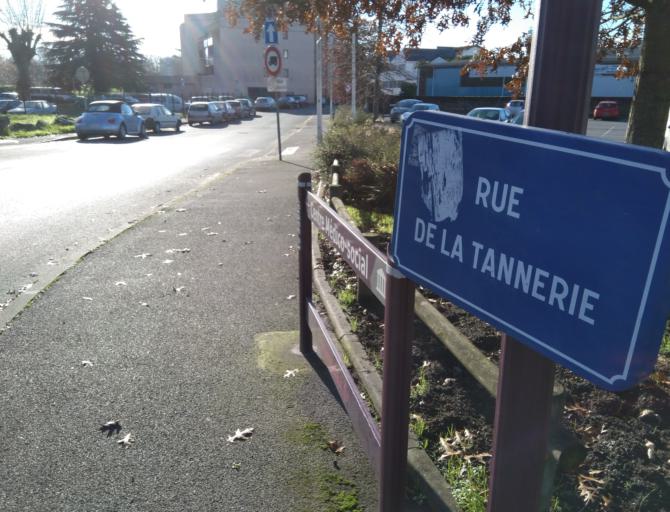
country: FR
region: Aquitaine
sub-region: Departement des Landes
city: Dax
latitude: 43.7153
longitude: -1.0529
